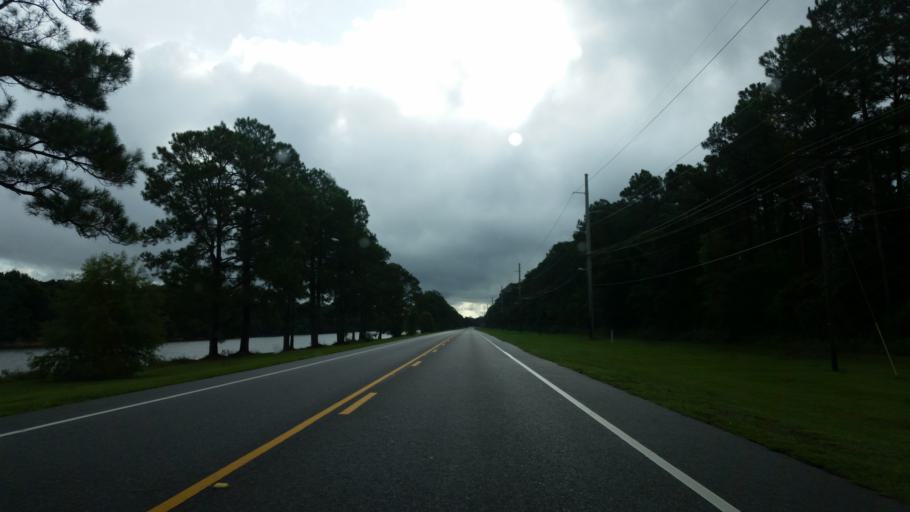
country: US
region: Alabama
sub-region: Baldwin County
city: Gulf Shores
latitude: 30.2793
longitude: -87.6663
